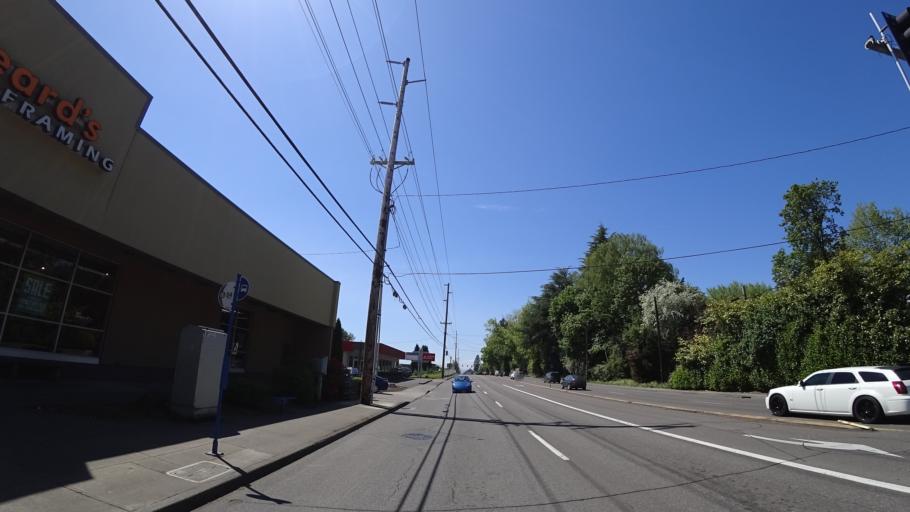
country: US
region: Oregon
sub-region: Washington County
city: Raleigh Hills
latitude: 45.4861
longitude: -122.7571
